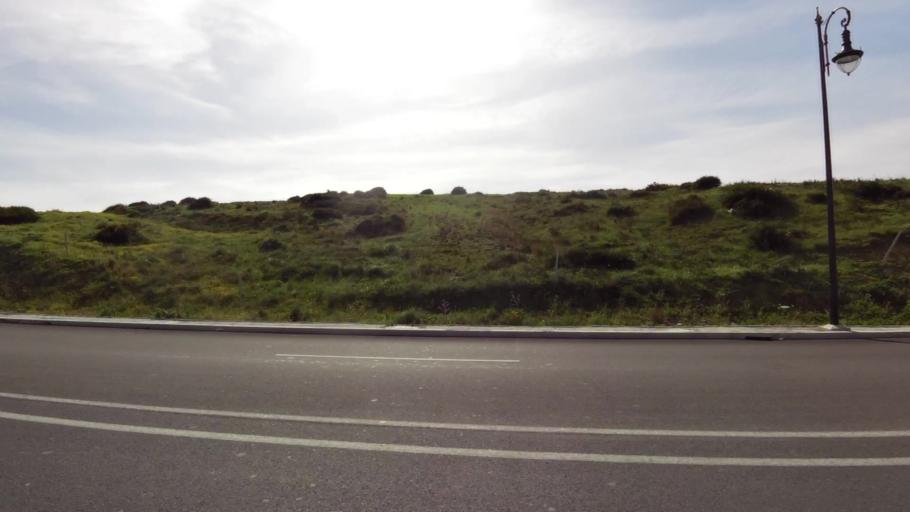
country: MA
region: Tanger-Tetouan
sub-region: Tanger-Assilah
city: Tangier
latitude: 35.7075
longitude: -5.7820
